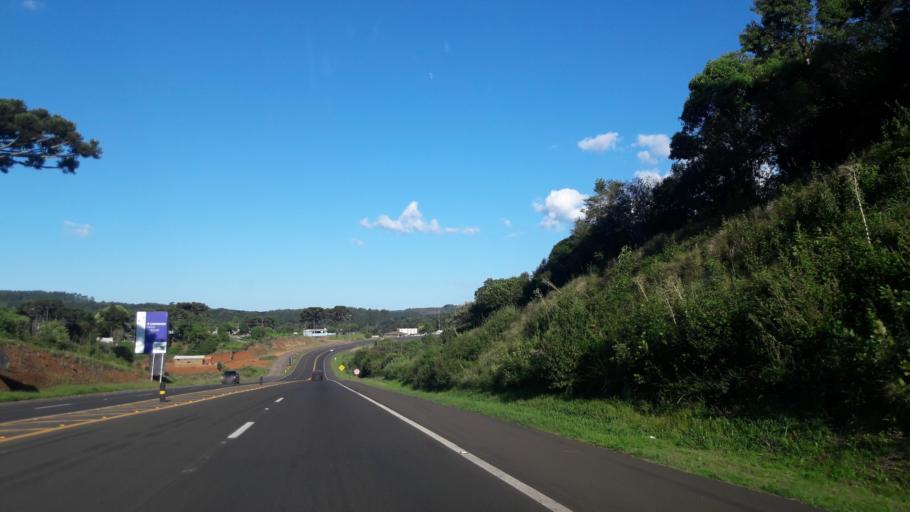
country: BR
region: Parana
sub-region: Guarapuava
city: Guarapuava
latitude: -25.3531
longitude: -51.3708
